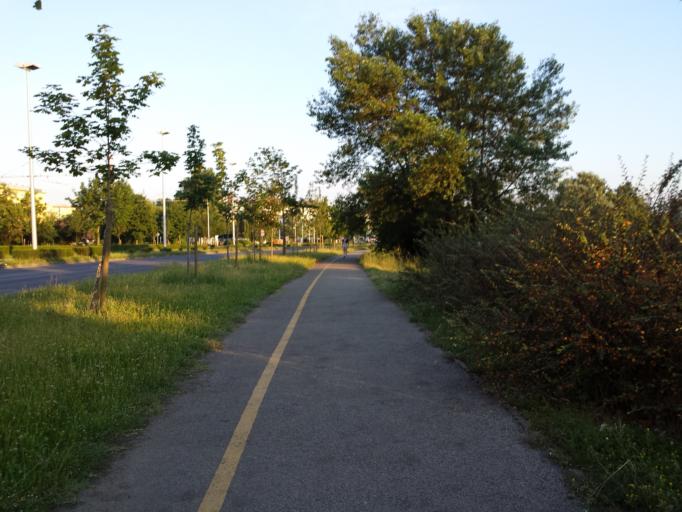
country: HR
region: Grad Zagreb
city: Novi Zagreb
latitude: 45.7906
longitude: 16.0032
